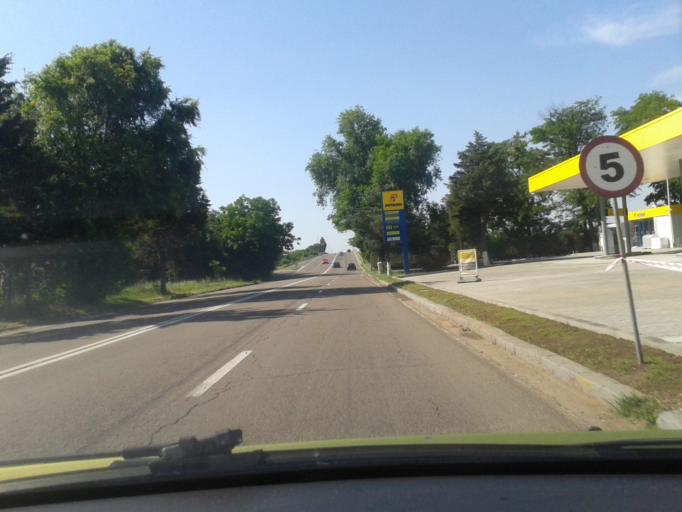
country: RO
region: Constanta
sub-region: Comuna Douazeci si Trei August
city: Dulcesti
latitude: 43.8620
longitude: 28.5754
